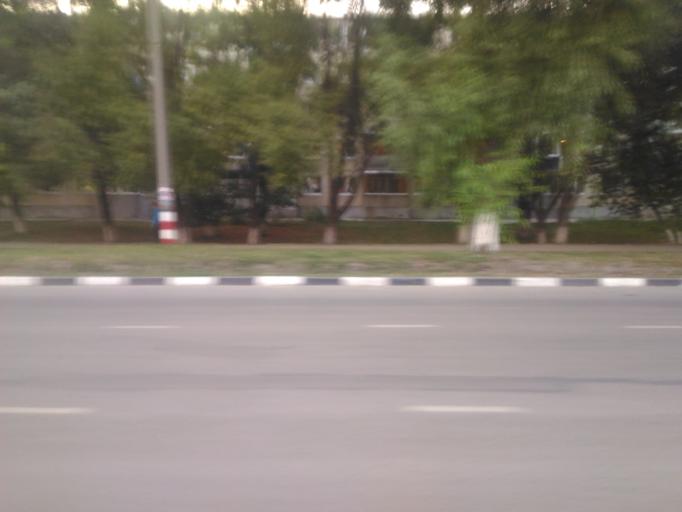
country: RU
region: Ulyanovsk
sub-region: Ulyanovskiy Rayon
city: Ulyanovsk
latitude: 54.2734
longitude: 48.2883
